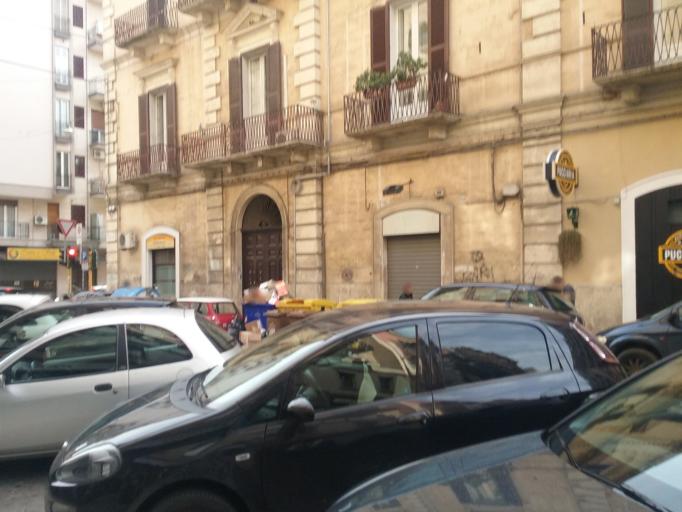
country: IT
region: Apulia
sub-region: Provincia di Bari
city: Bari
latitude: 41.1243
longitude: 16.8639
